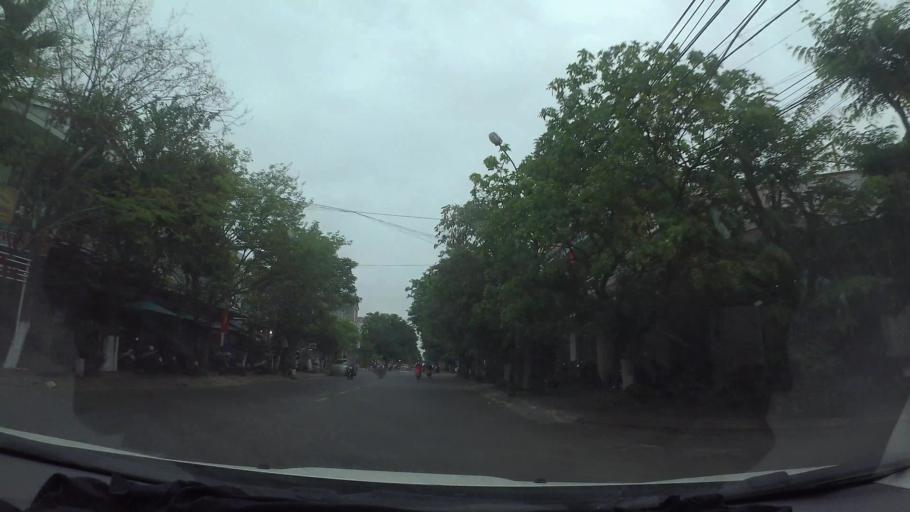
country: VN
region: Da Nang
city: Lien Chieu
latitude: 16.0772
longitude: 108.1600
